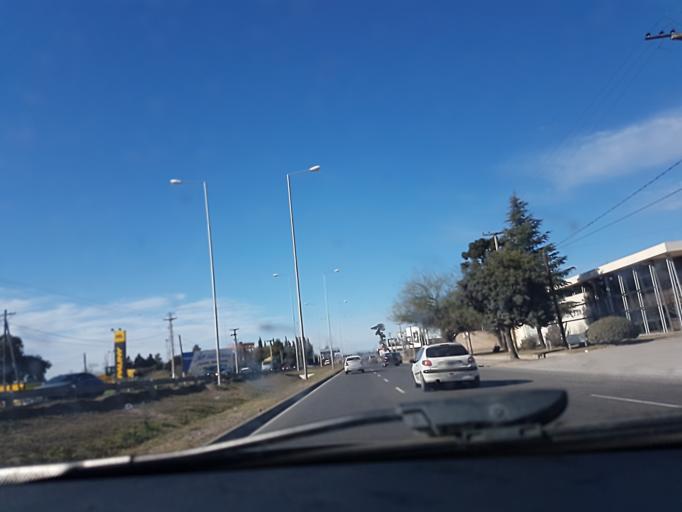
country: AR
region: Cordoba
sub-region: Departamento de Capital
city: Cordoba
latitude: -31.3463
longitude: -64.2061
